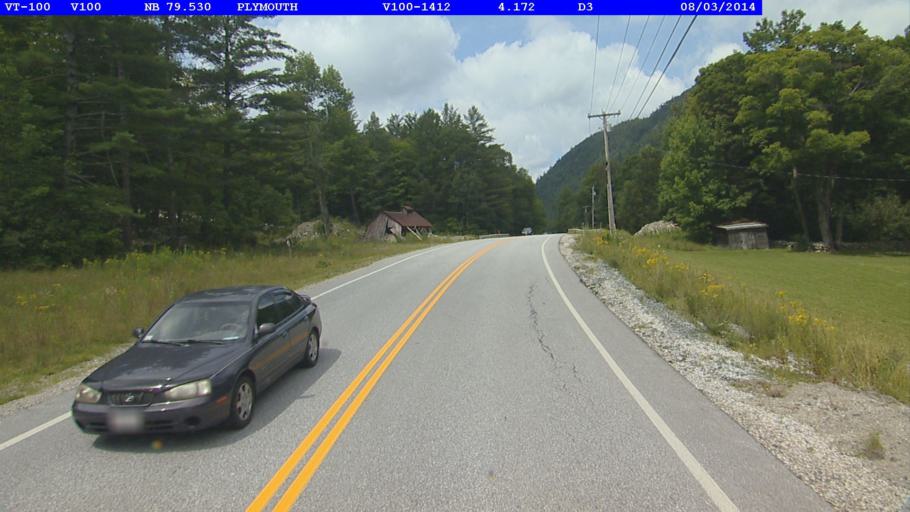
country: US
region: Vermont
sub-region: Windsor County
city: Woodstock
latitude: 43.5148
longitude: -72.7315
